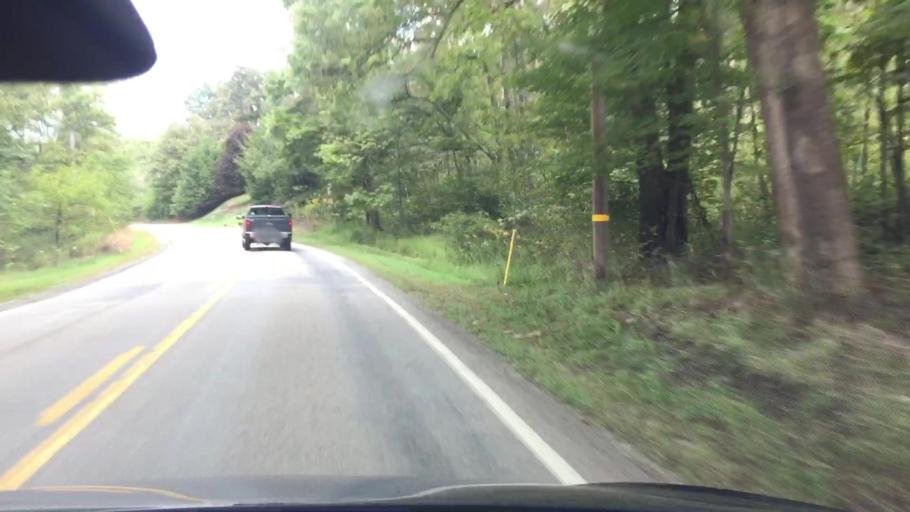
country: US
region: Pennsylvania
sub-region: Allegheny County
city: Curtisville
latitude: 40.6969
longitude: -79.8412
